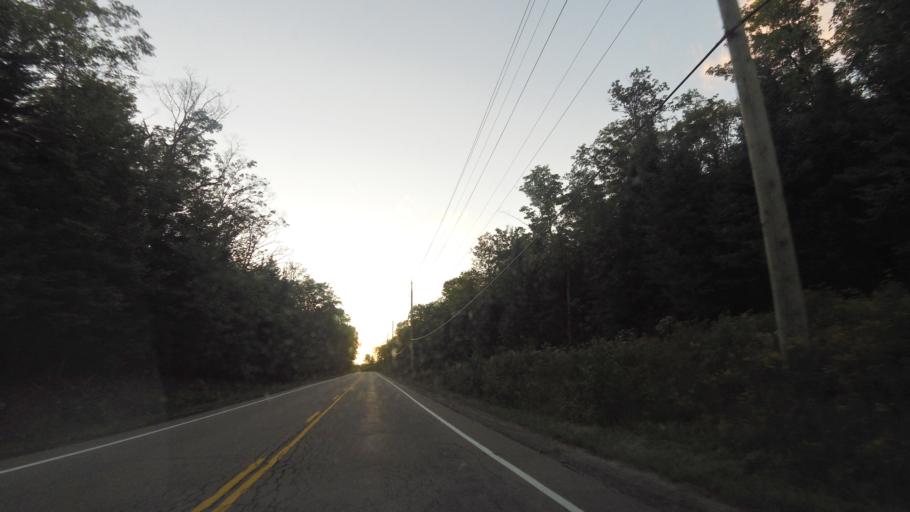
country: CA
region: Ontario
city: Bancroft
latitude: 45.0276
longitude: -78.3892
